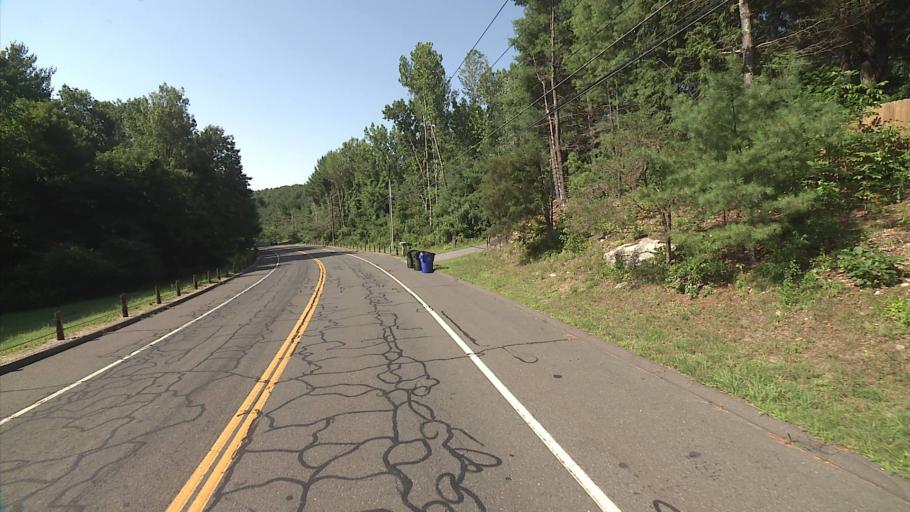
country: US
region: Connecticut
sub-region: Litchfield County
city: Winsted
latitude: 41.9750
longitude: -73.0176
